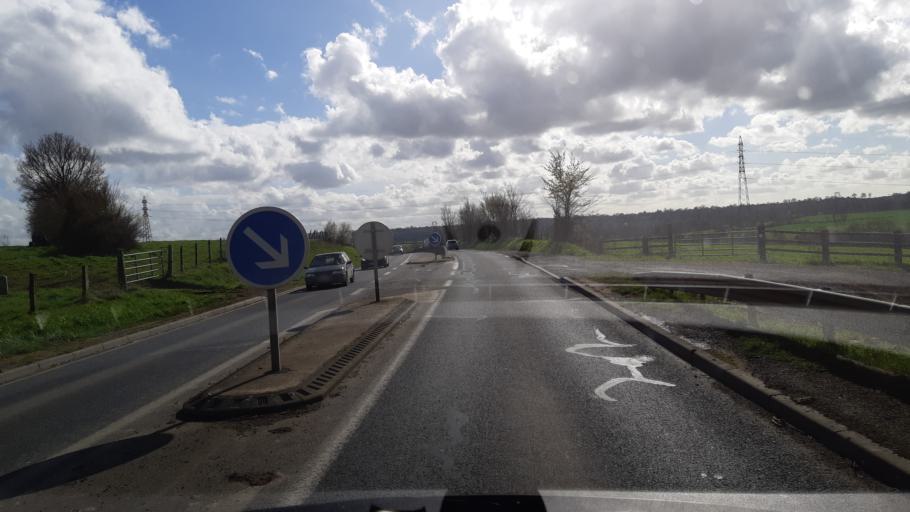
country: FR
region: Lower Normandy
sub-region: Departement de la Manche
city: Agneaux
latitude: 49.0986
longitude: -1.1197
